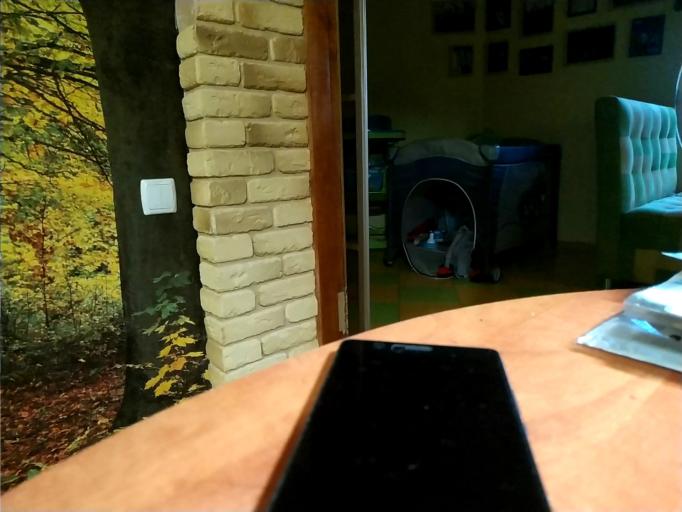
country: RU
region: Orjol
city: Znamenskoye
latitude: 53.4279
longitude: 35.5347
